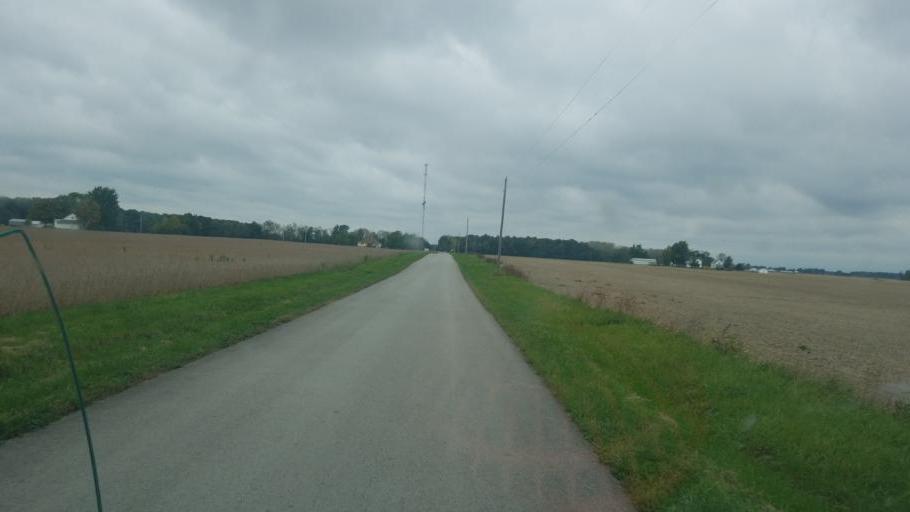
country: US
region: Ohio
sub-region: Seneca County
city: Fostoria
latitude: 41.0794
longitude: -83.5101
